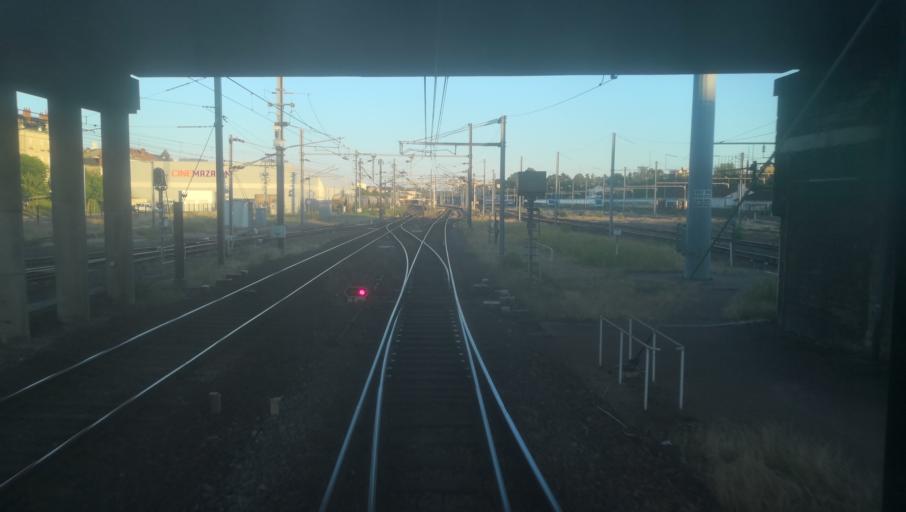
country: FR
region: Bourgogne
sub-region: Departement de la Nievre
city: Nevers
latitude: 46.9925
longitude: 3.1478
